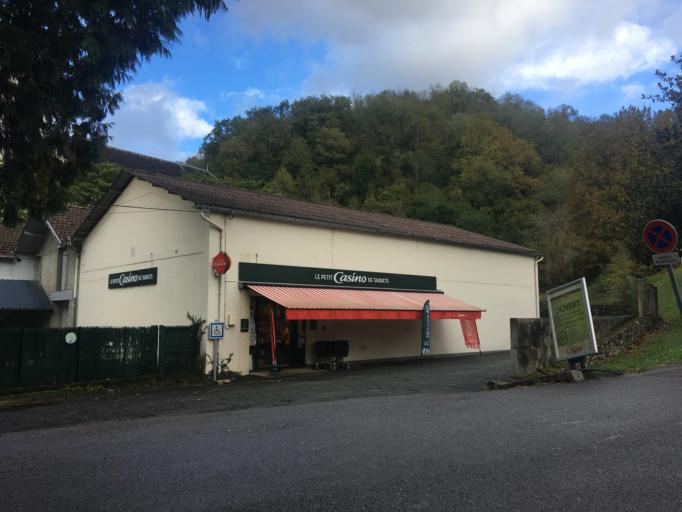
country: FR
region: Aquitaine
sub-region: Departement des Pyrenees-Atlantiques
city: Mauleon-Licharre
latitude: 43.1173
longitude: -0.8638
